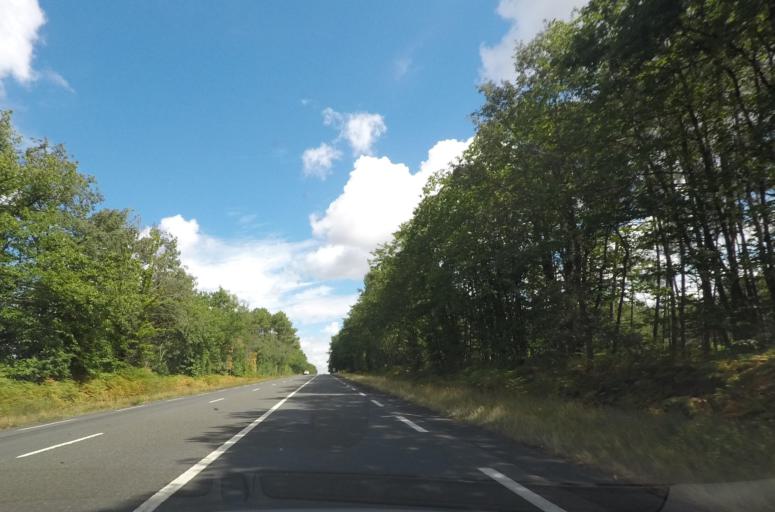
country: FR
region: Pays de la Loire
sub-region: Departement de la Sarthe
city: Cerans-Foulletourte
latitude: 47.8089
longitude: 0.0584
